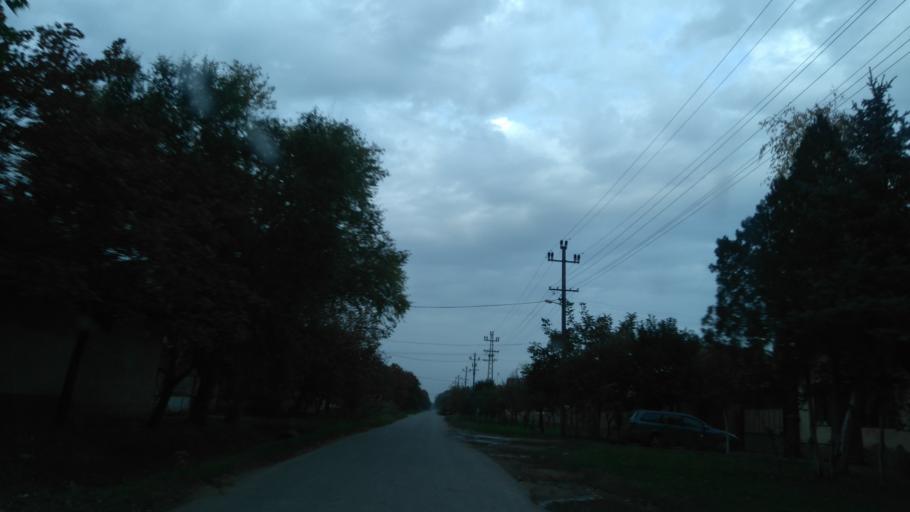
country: RS
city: Mol
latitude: 45.7600
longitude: 20.1368
